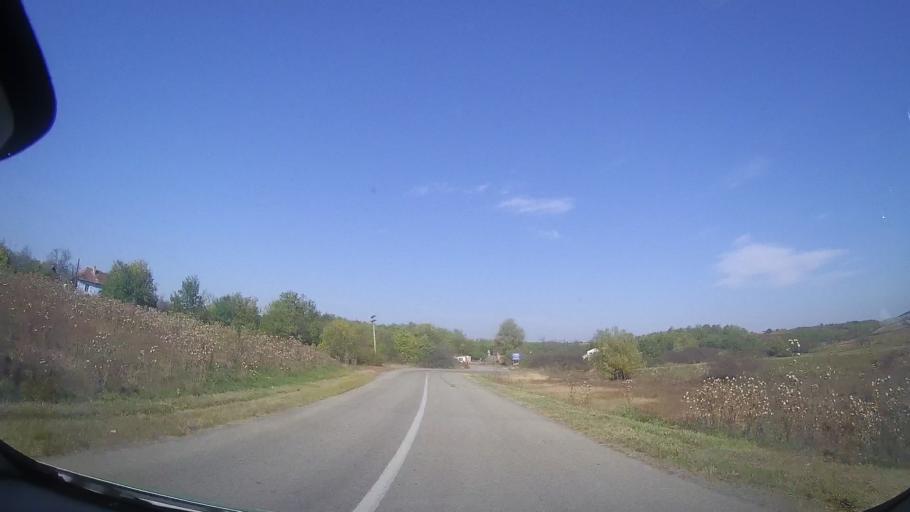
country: RO
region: Timis
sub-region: Comuna Ghizela
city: Ghizela
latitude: 45.8074
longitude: 21.7208
